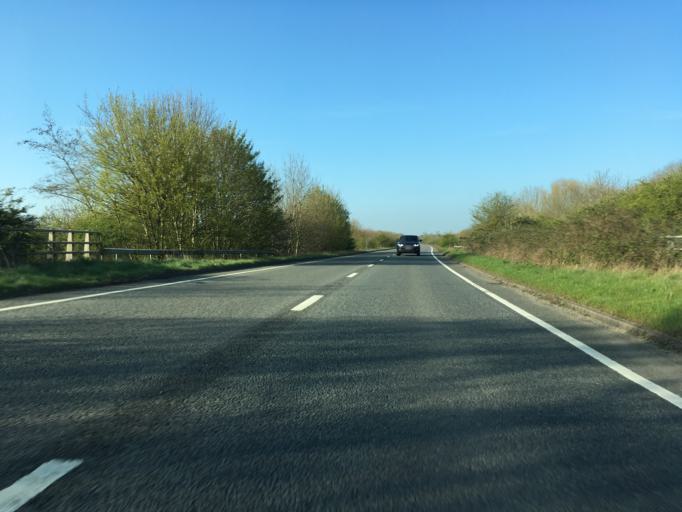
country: GB
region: England
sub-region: Northamptonshire
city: Deanshanger
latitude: 52.0481
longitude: -0.8764
